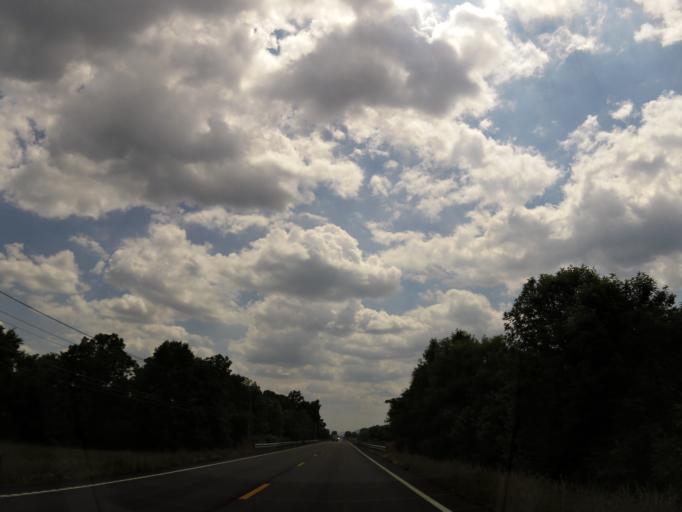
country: US
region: Tennessee
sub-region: Sequatchie County
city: Dunlap
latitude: 35.4947
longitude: -85.2982
